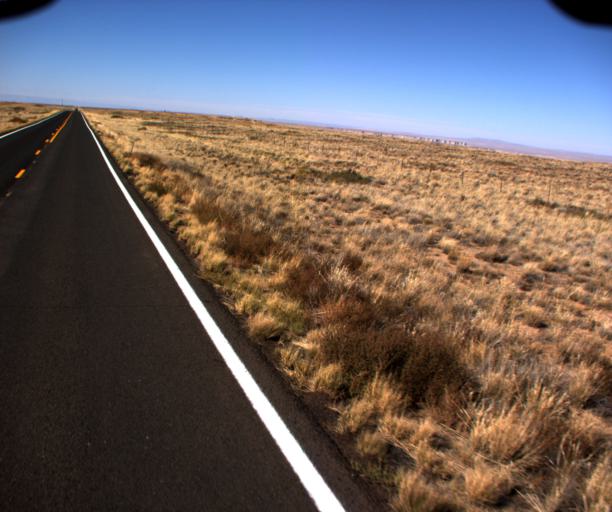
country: US
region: Arizona
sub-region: Coconino County
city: Tuba City
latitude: 35.9712
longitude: -110.9646
